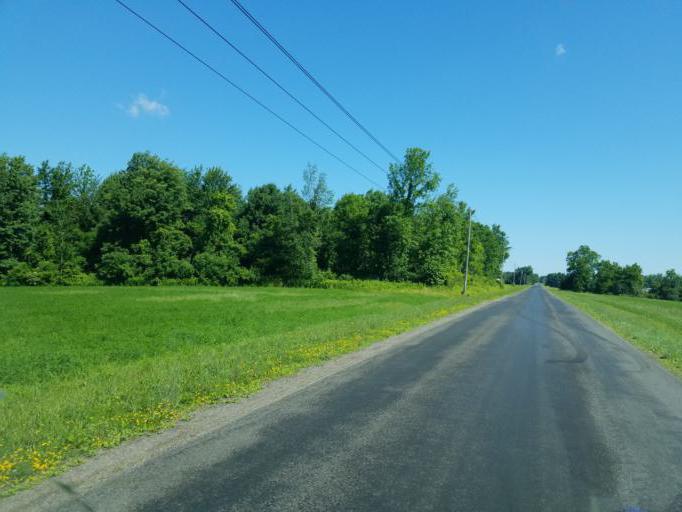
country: US
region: New York
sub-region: Wayne County
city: Wolcott
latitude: 43.1773
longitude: -76.8667
